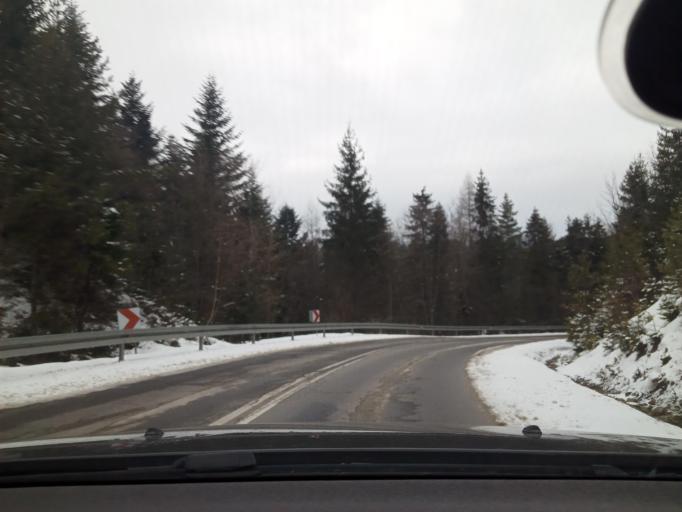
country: PL
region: Lesser Poland Voivodeship
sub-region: Powiat nowotarski
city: Krosnica
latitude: 49.4194
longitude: 20.3425
